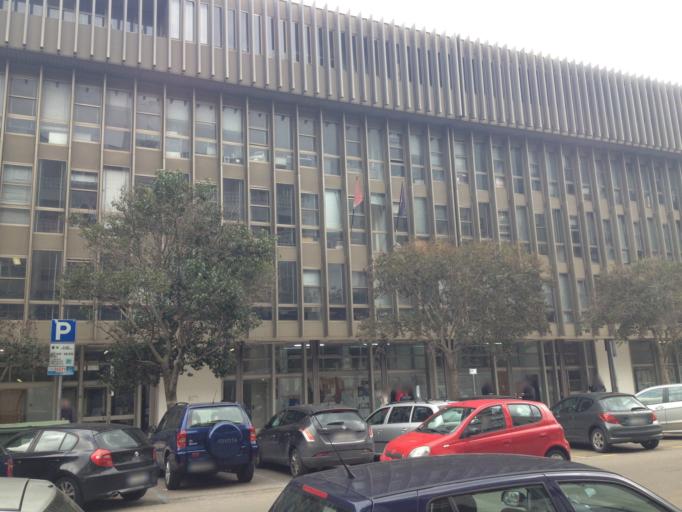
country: IT
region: Apulia
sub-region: Provincia di Lecce
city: Lecce
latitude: 40.3604
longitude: 18.1724
